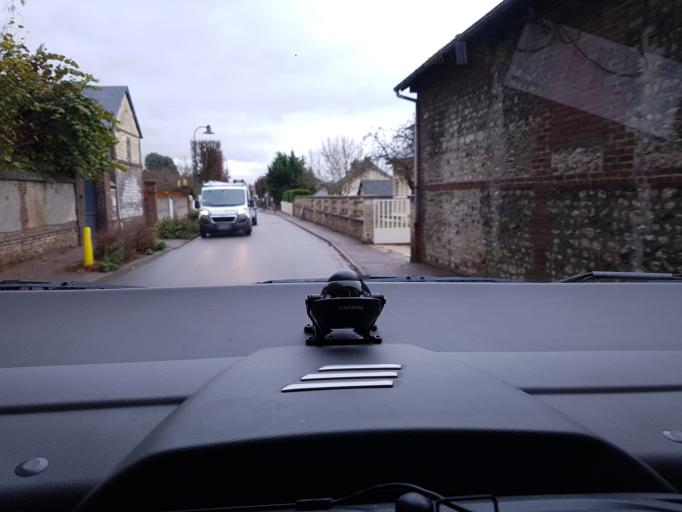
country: FR
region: Haute-Normandie
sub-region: Departement de l'Eure
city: Alizay
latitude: 49.3191
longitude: 1.1636
